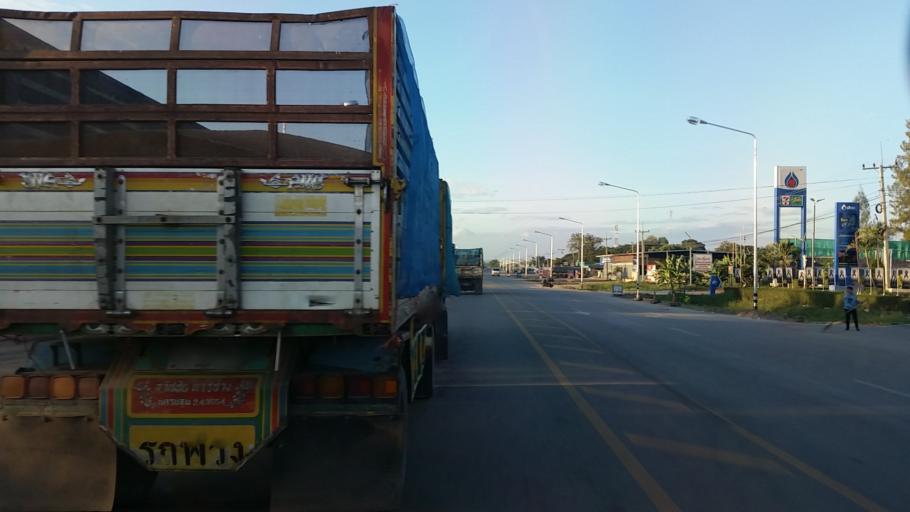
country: TH
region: Lop Buri
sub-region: Amphoe Lam Sonthi
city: Lam Sonthi
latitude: 15.2815
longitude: 101.3469
